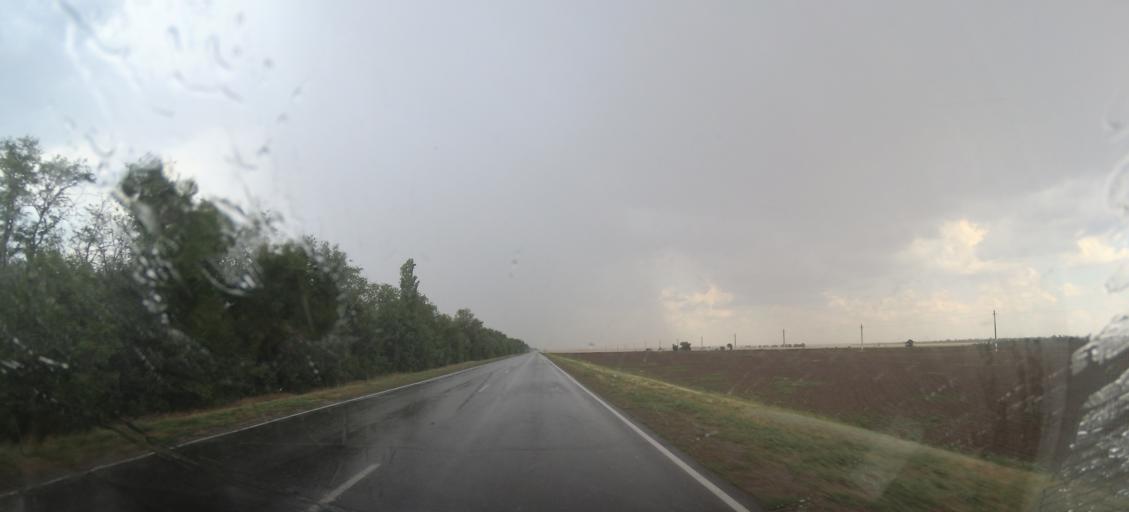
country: RU
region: Rostov
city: Proletarsk
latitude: 46.6581
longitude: 41.6833
